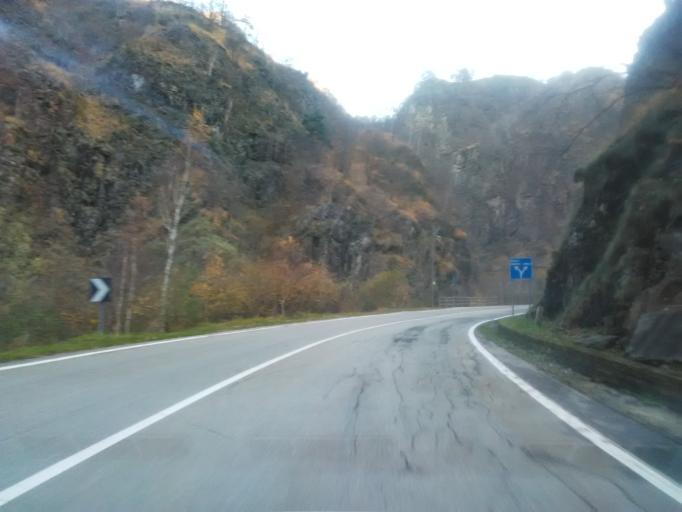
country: IT
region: Piedmont
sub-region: Provincia di Vercelli
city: Cervatto
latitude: 45.8783
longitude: 8.1753
